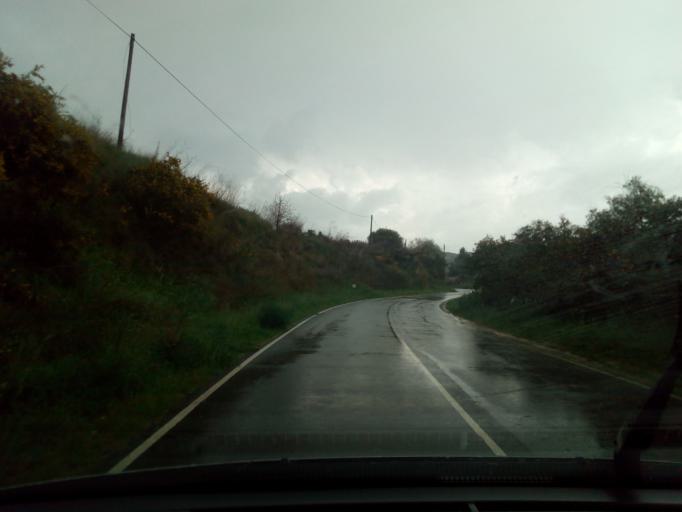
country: CY
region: Pafos
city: Polis
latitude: 34.9816
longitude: 32.4574
